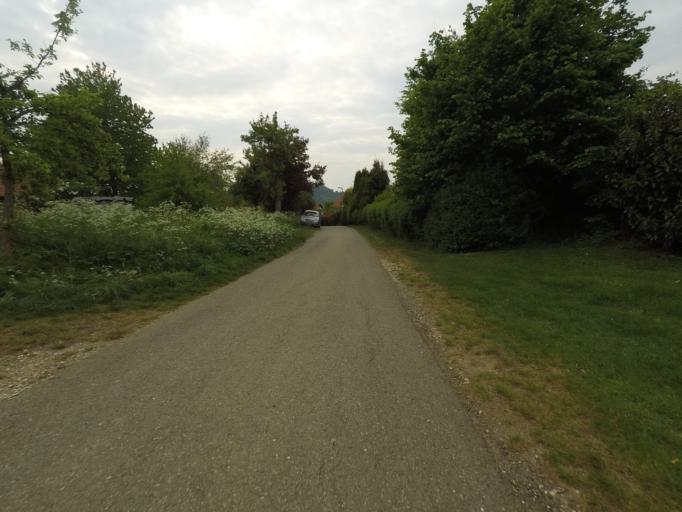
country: DE
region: Baden-Wuerttemberg
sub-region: Tuebingen Region
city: Pfullingen
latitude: 48.4627
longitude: 9.2369
